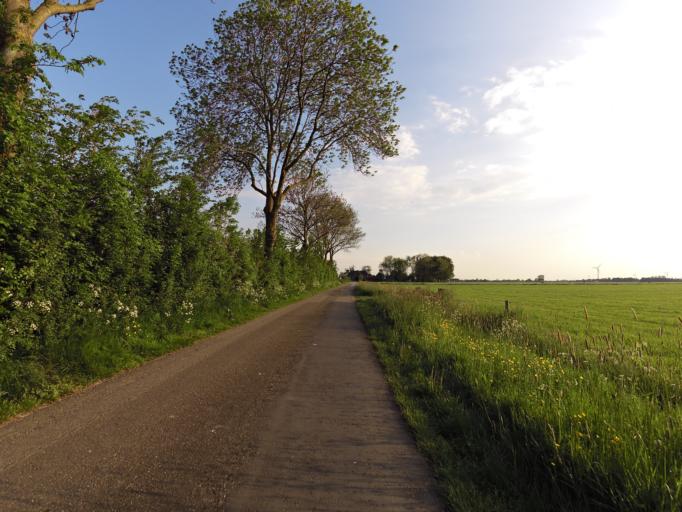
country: NL
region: Gelderland
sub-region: Oude IJsselstreek
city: Gendringen
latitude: 51.8529
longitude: 6.3559
